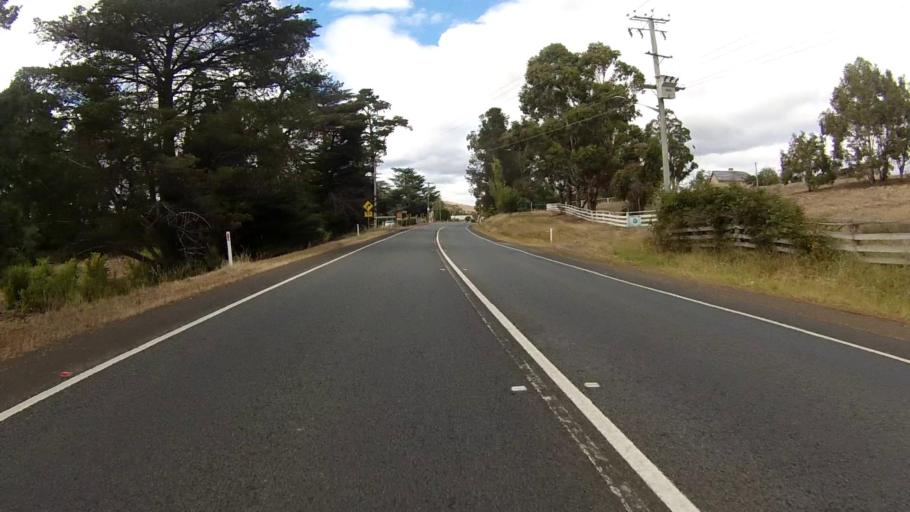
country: AU
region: Tasmania
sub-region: Brighton
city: Bridgewater
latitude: -42.6787
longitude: 147.2650
